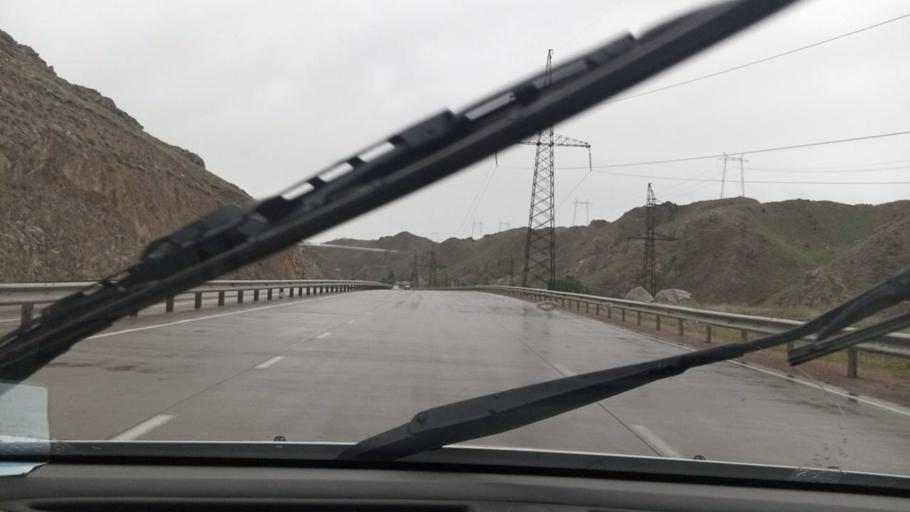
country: TJ
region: Viloyati Sughd
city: Shaydon
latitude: 40.9723
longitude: 70.6535
